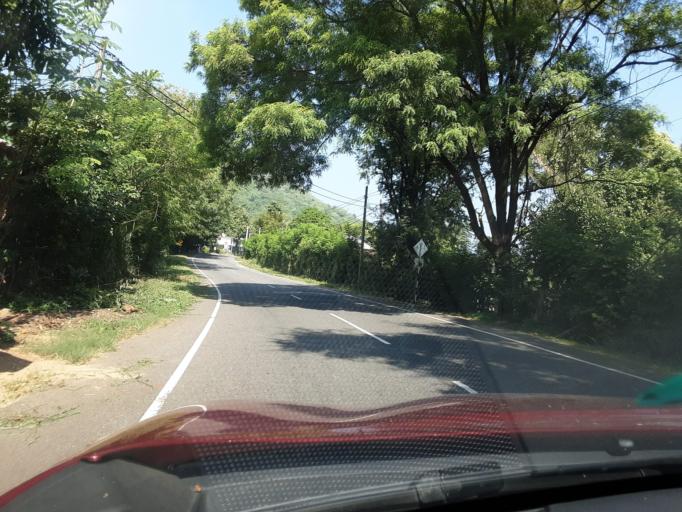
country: LK
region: Uva
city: Badulla
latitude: 7.1664
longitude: 81.0525
